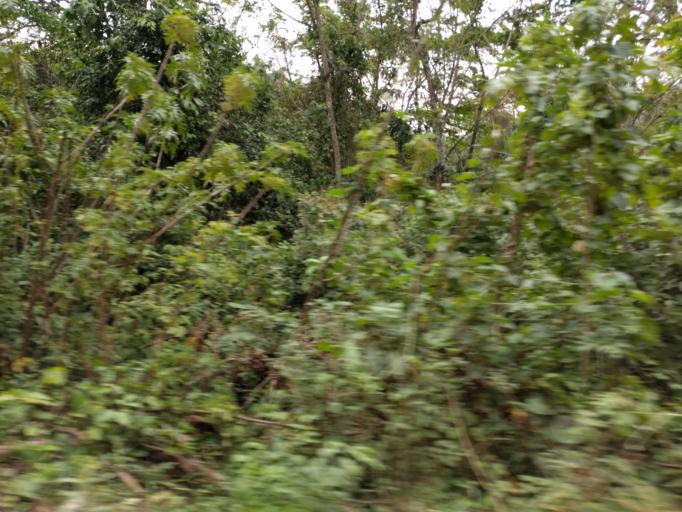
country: BO
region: Santa Cruz
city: Santiago del Torno
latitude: -17.9159
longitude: -63.4277
